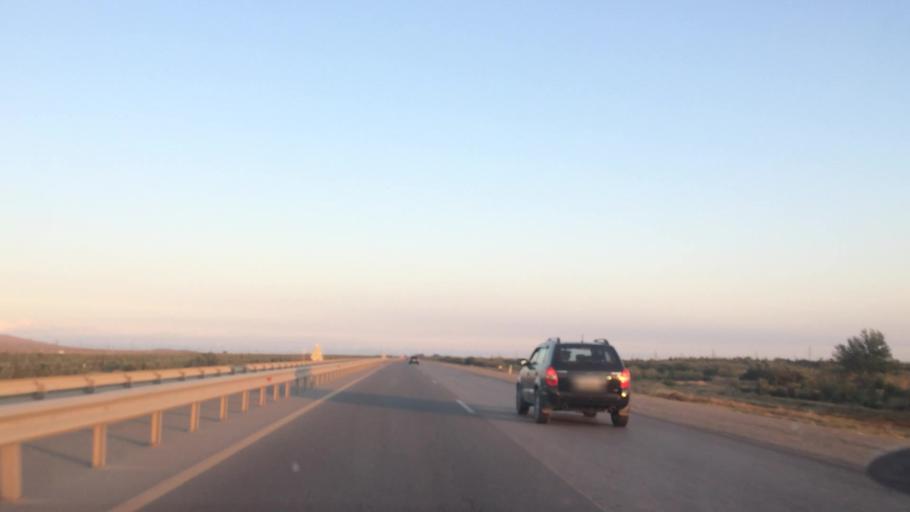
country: AZ
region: Baki
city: Qobustan
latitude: 39.9617
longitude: 49.2894
